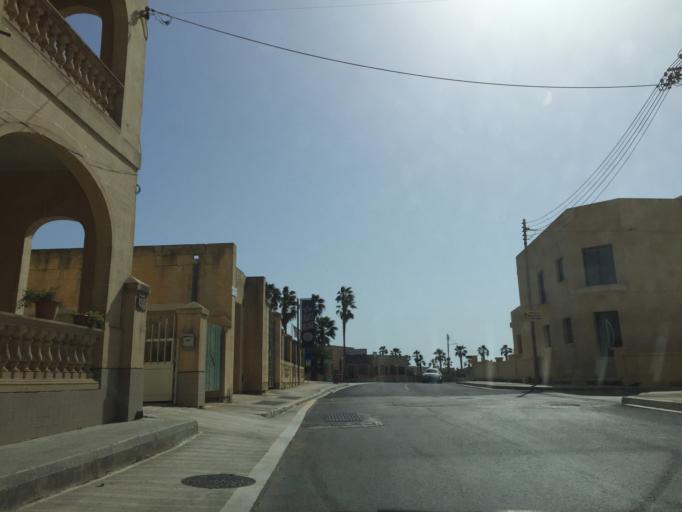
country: MT
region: L-Gharb
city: Gharb
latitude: 36.0554
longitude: 14.2111
